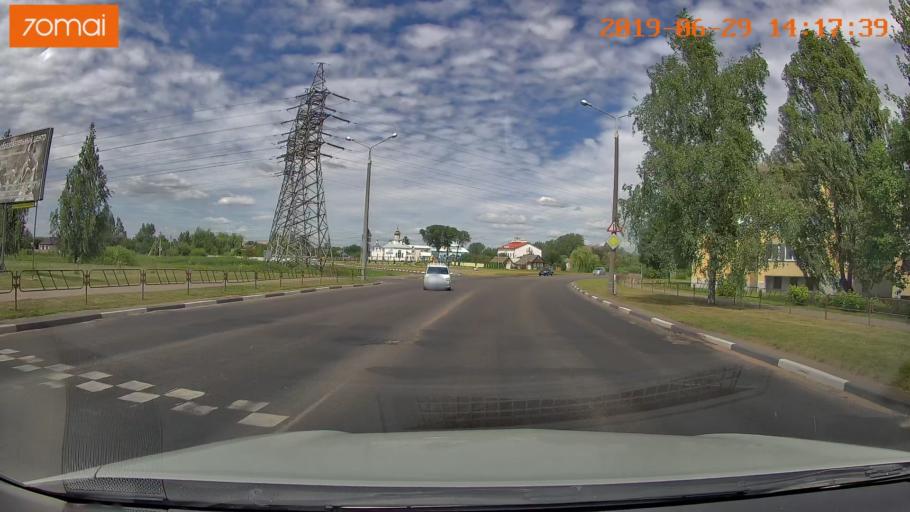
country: BY
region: Minsk
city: Salihorsk
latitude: 52.7997
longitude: 27.5401
